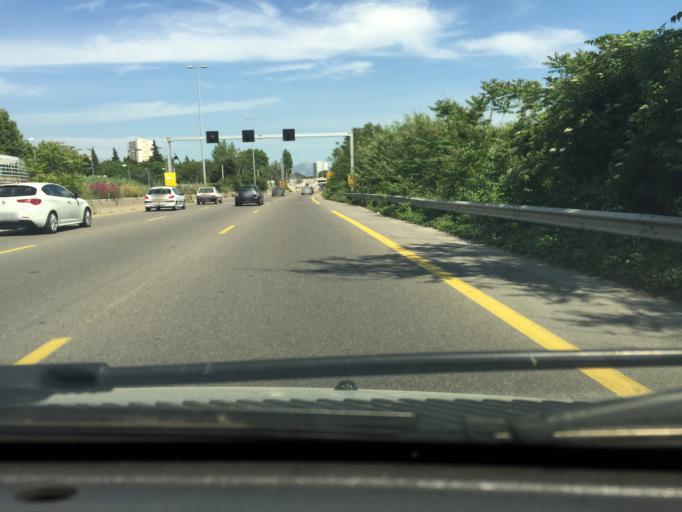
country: FR
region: Provence-Alpes-Cote d'Azur
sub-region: Departement des Bouches-du-Rhone
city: Marseille 10
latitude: 43.2849
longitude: 5.4186
